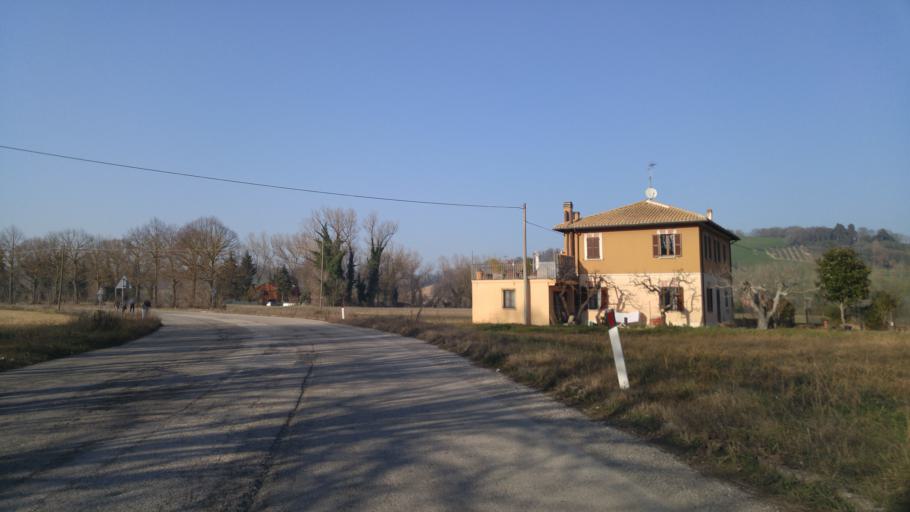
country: IT
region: The Marches
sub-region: Provincia di Pesaro e Urbino
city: Fenile
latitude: 43.8301
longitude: 12.9166
